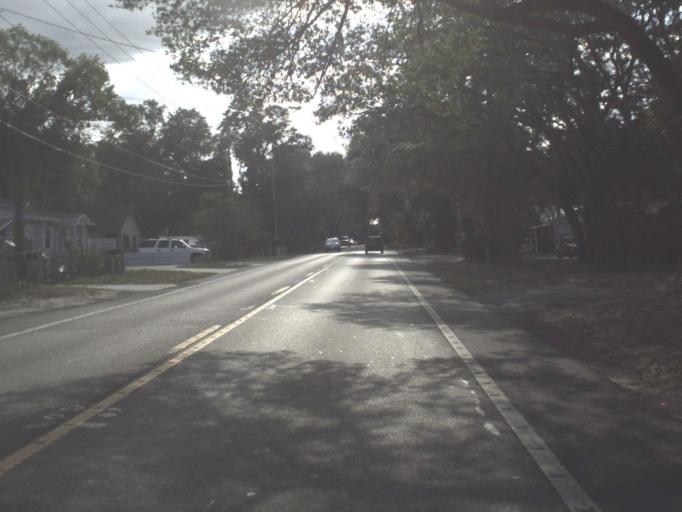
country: US
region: Florida
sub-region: Lake County
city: Mount Plymouth
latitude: 28.8078
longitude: -81.5650
